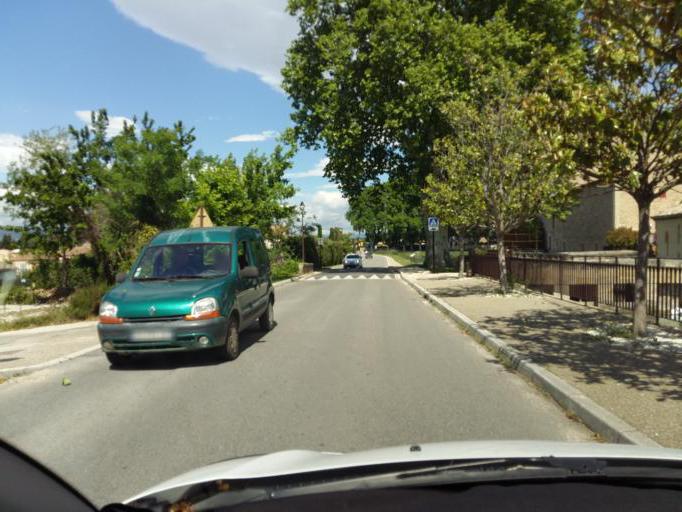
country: FR
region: Provence-Alpes-Cote d'Azur
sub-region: Departement du Vaucluse
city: Taillades
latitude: 43.8381
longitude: 5.0879
